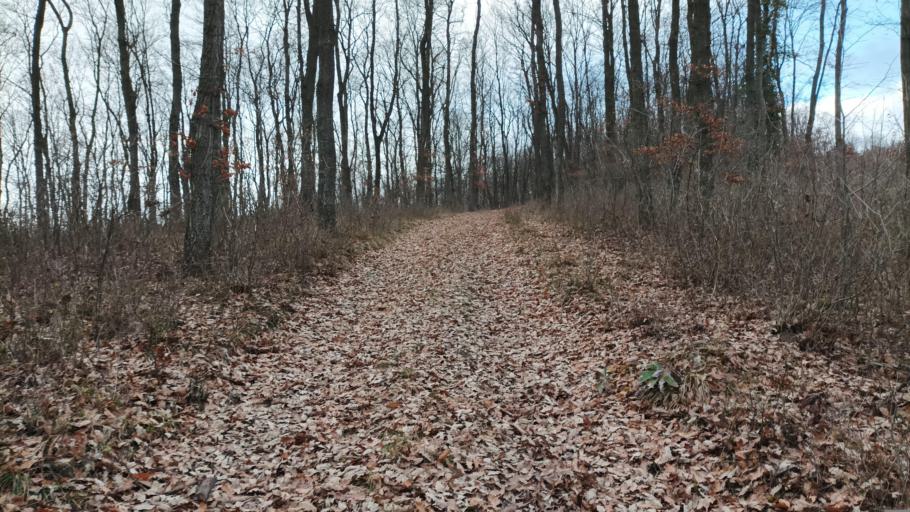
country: HU
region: Tolna
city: Szentgalpuszta
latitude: 46.3327
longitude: 18.6217
